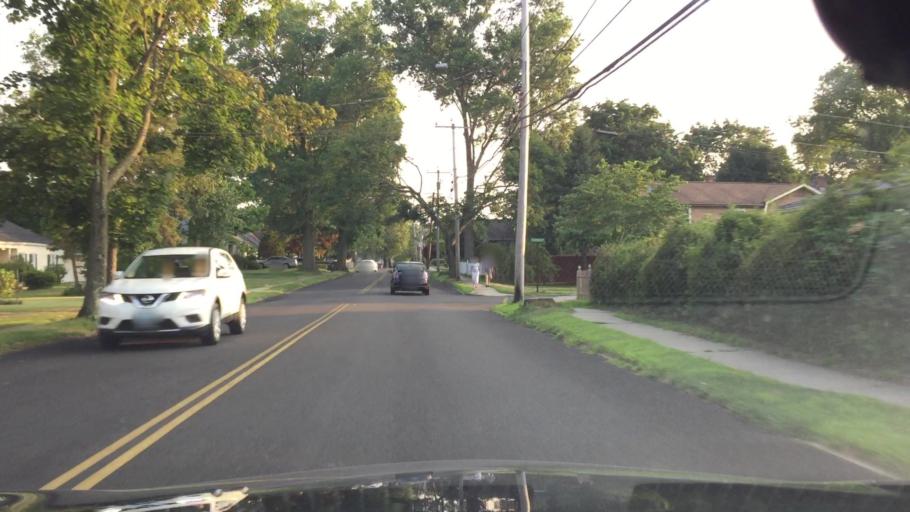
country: US
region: Connecticut
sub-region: New Haven County
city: City of Milford (balance)
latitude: 41.1993
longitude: -73.0918
